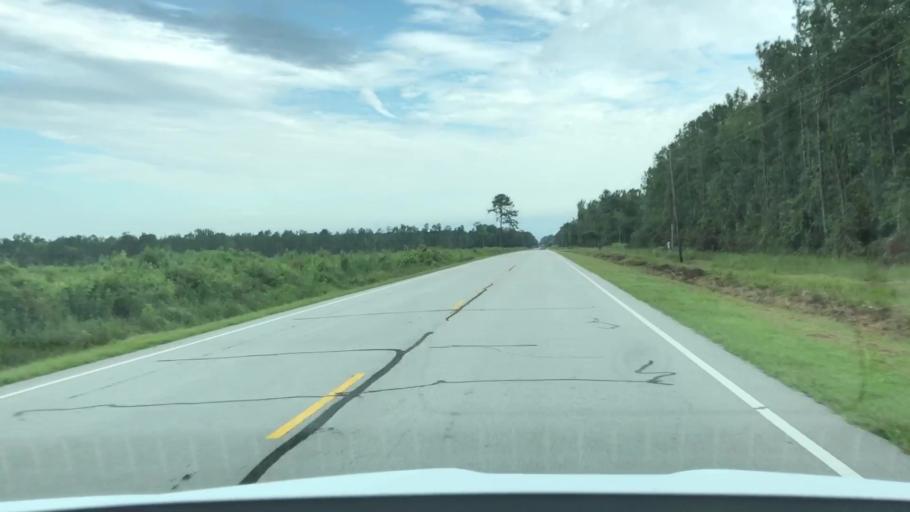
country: US
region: North Carolina
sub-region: Lenoir County
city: Kinston
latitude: 35.1259
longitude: -77.5206
